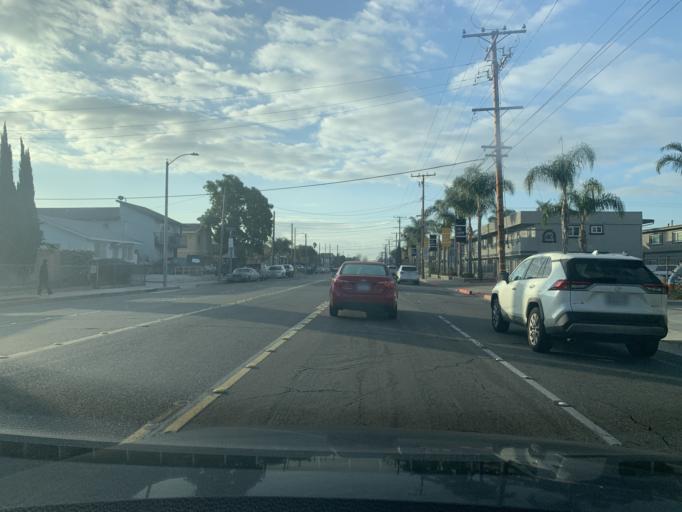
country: US
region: California
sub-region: Orange County
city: Westminster
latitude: 33.7630
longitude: -118.0160
